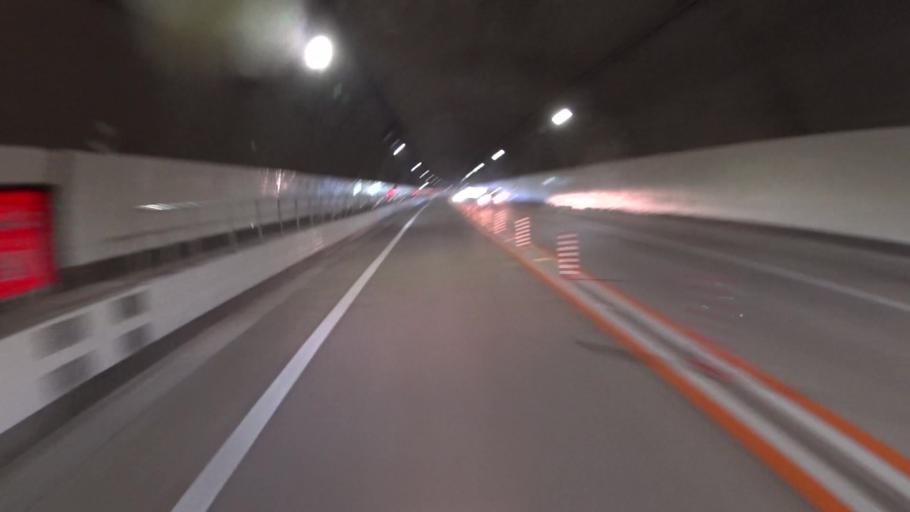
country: JP
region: Kyoto
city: Ayabe
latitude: 35.2369
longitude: 135.3438
